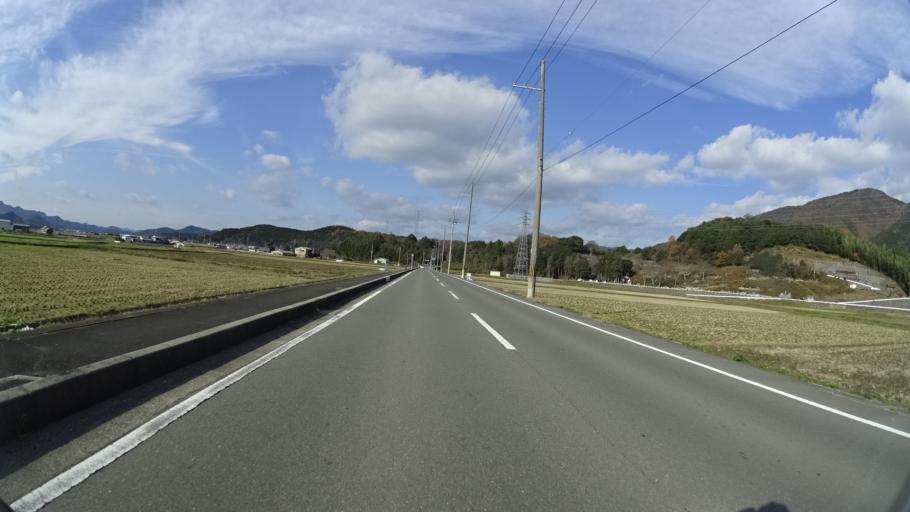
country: JP
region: Kyoto
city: Kameoka
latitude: 35.0603
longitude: 135.5679
